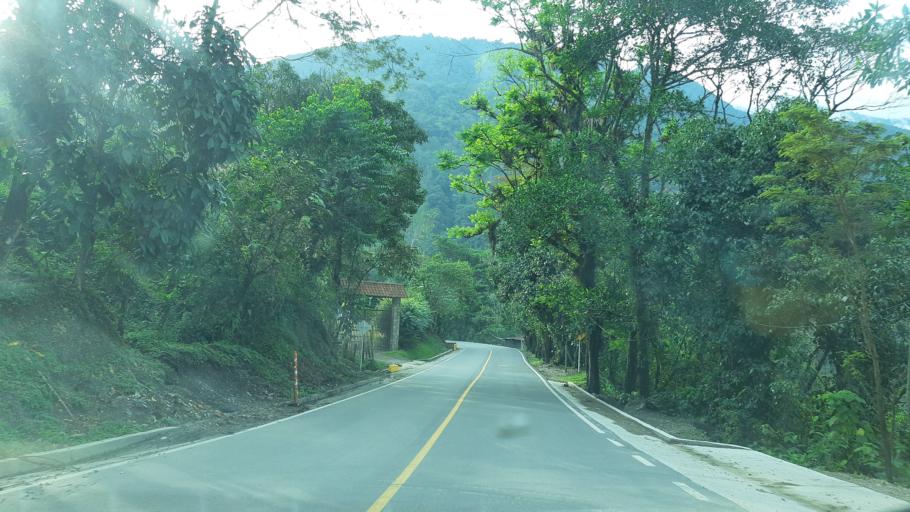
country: CO
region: Boyaca
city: Santa Maria
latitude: 4.8669
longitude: -73.2505
